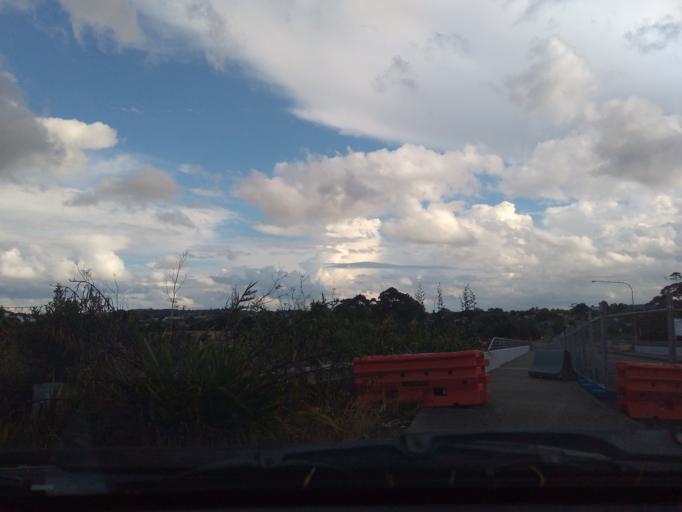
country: NZ
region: Auckland
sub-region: Auckland
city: Manukau City
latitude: -36.9953
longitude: 174.8810
